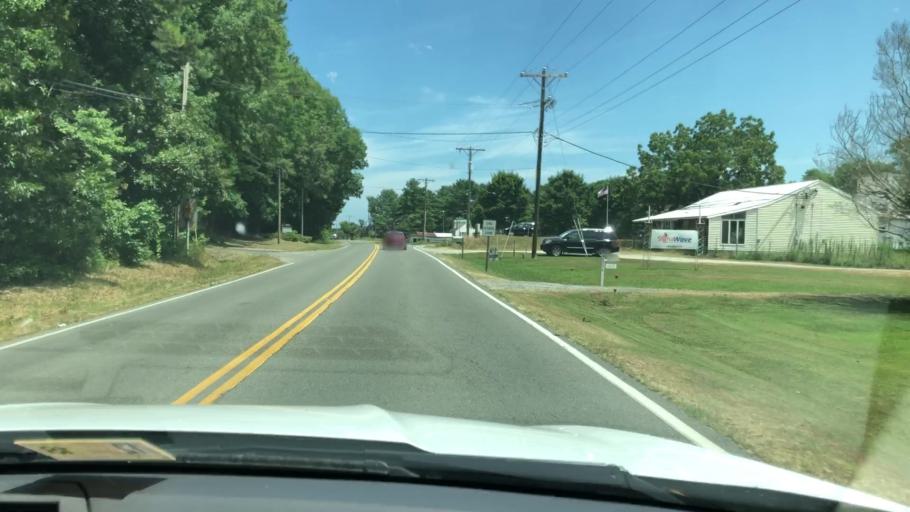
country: US
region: Virginia
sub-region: Lancaster County
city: Lancaster
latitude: 37.7678
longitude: -76.4535
